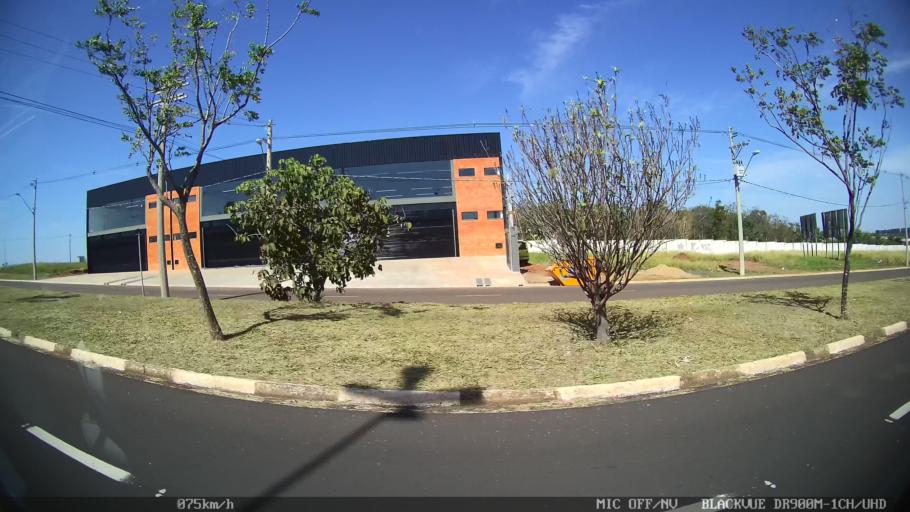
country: BR
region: Sao Paulo
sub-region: Franca
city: Franca
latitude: -20.5515
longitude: -47.4321
